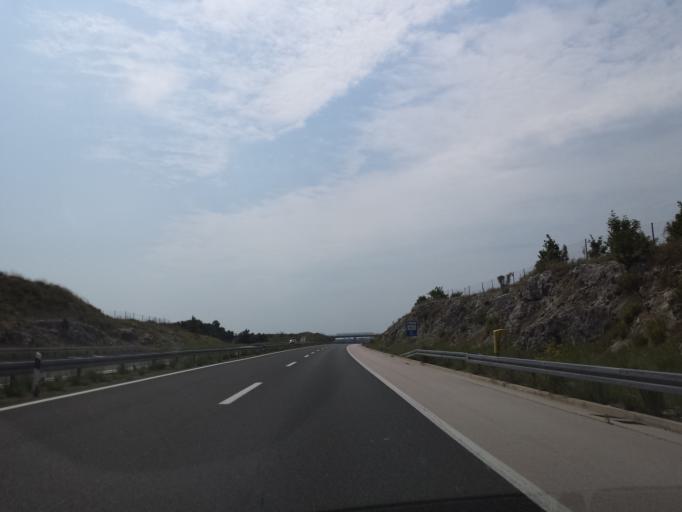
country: HR
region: Zadarska
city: Policnik
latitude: 44.1757
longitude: 15.4272
